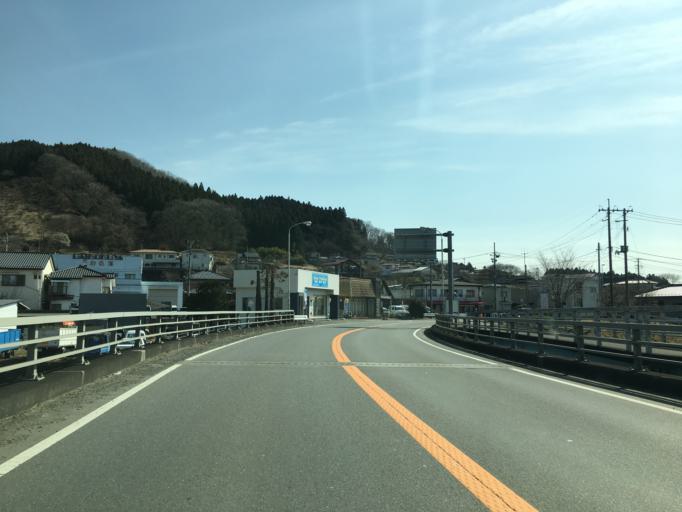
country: JP
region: Ibaraki
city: Daigo
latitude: 36.9521
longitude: 140.4153
